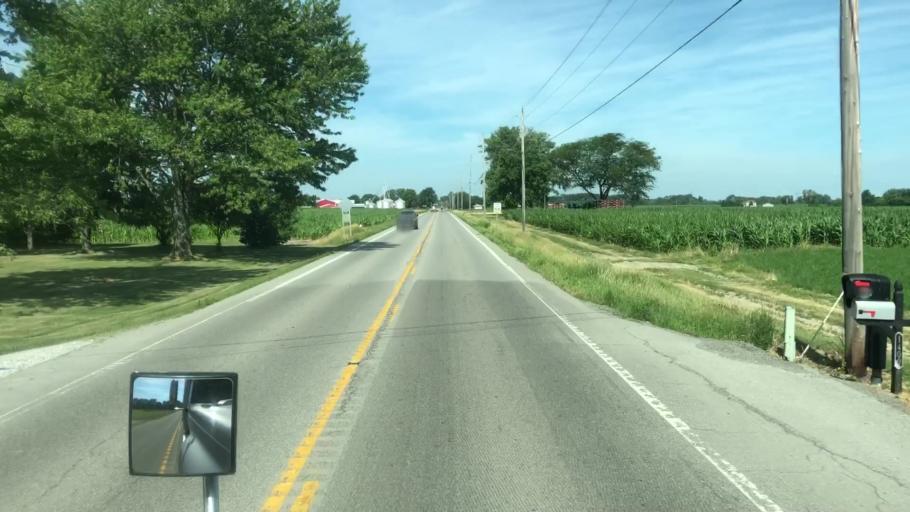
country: US
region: Ohio
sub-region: Erie County
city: Sandusky
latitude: 41.4405
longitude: -82.7886
